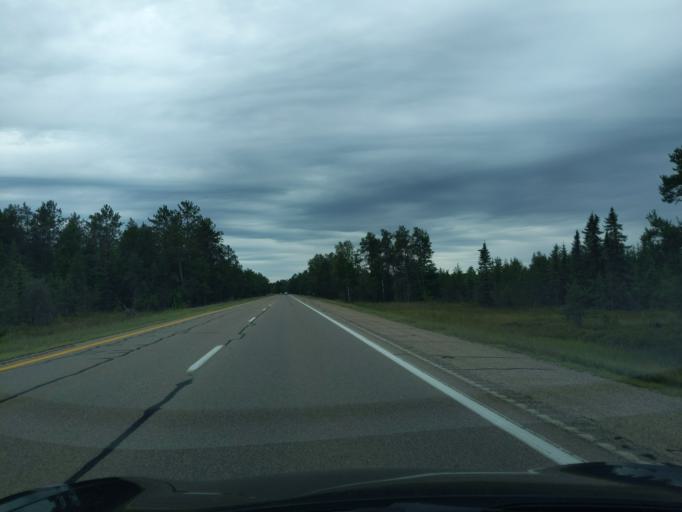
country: US
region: Michigan
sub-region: Roscommon County
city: Houghton Lake
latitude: 44.2432
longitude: -84.8039
